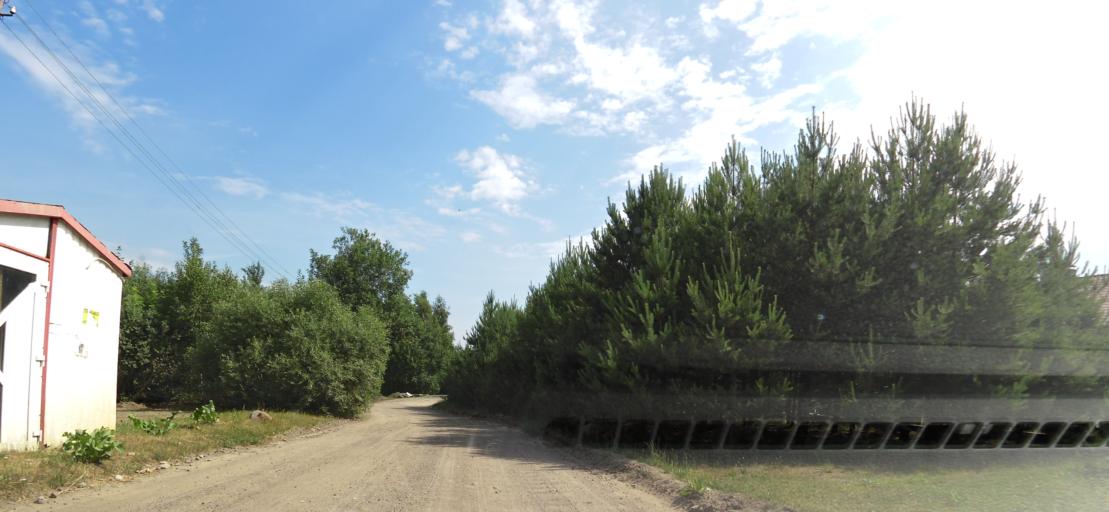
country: LT
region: Vilnius County
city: Pasilaiciai
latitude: 54.7476
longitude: 25.2266
